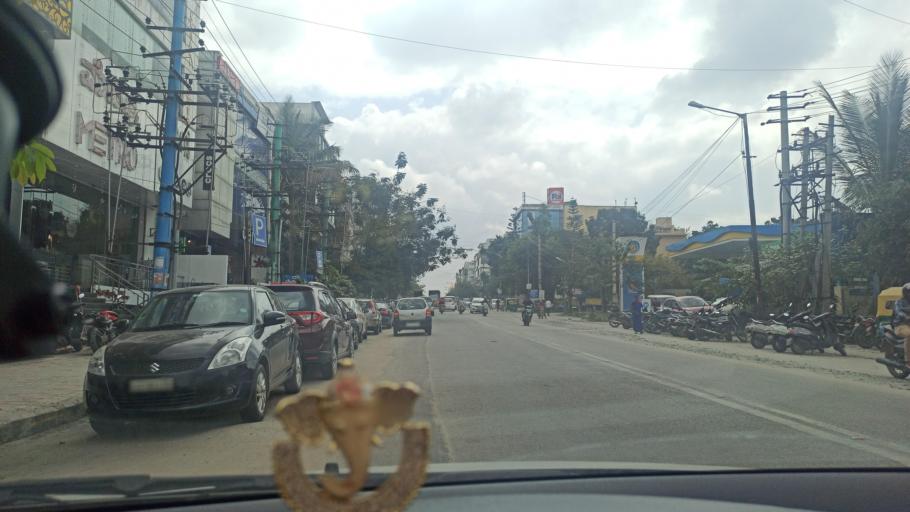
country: IN
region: Karnataka
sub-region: Bangalore Urban
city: Bangalore
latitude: 12.9204
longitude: 77.6517
